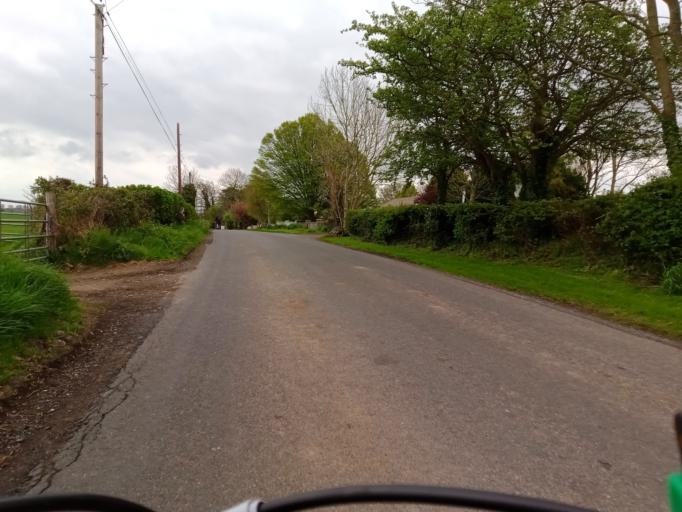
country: IE
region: Leinster
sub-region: Kilkenny
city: Kilkenny
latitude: 52.6192
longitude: -7.2696
